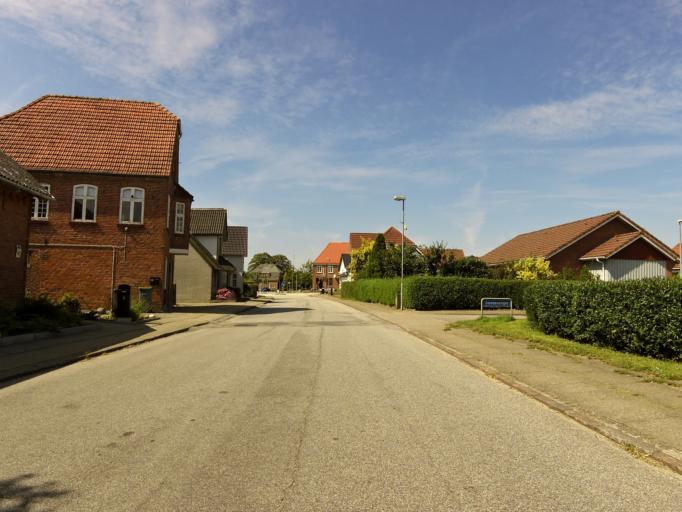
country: DK
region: South Denmark
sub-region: Haderslev Kommune
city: Gram
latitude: 55.2471
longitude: 8.9708
